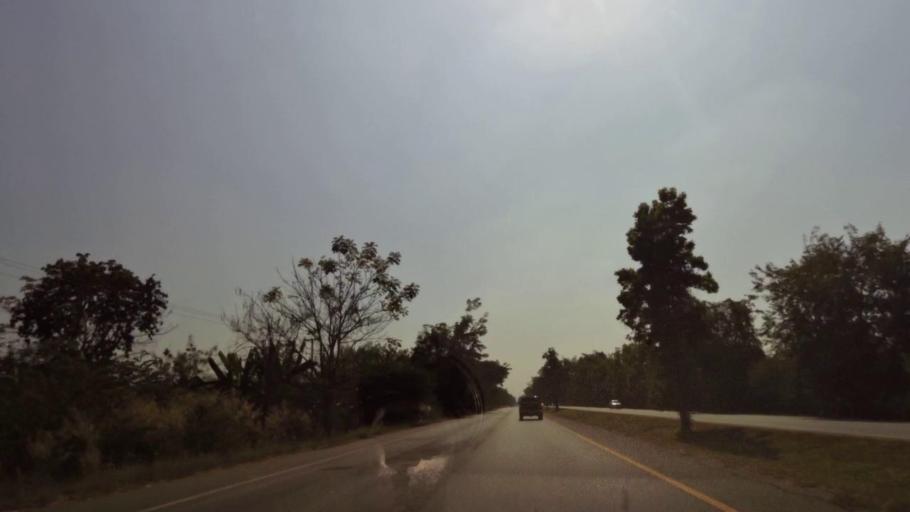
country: TH
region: Phichit
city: Bueng Na Rang
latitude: 16.3315
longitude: 100.1284
